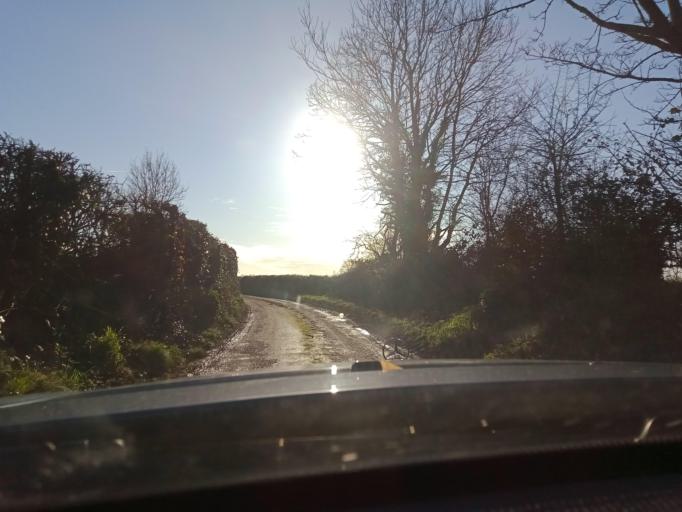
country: IE
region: Leinster
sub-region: Kilkenny
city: Mooncoin
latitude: 52.3006
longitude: -7.1941
